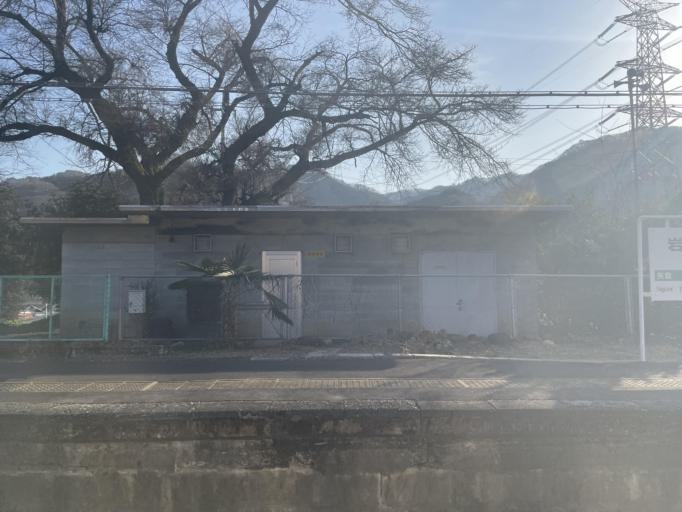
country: JP
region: Gunma
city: Nakanojomachi
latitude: 36.5634
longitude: 138.7595
